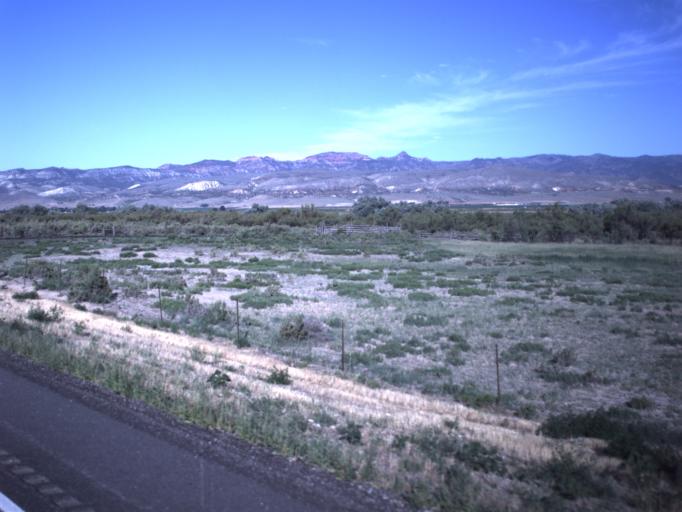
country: US
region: Utah
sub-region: Sevier County
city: Salina
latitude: 38.9407
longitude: -111.8864
